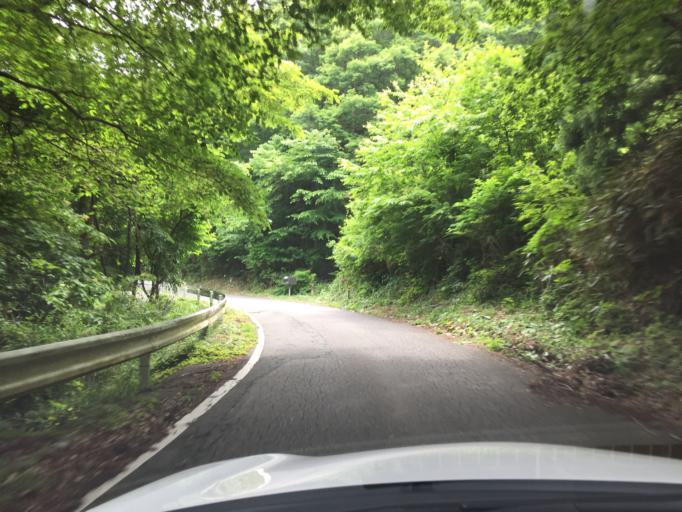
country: JP
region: Fukushima
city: Sukagawa
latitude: 37.2677
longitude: 140.5005
